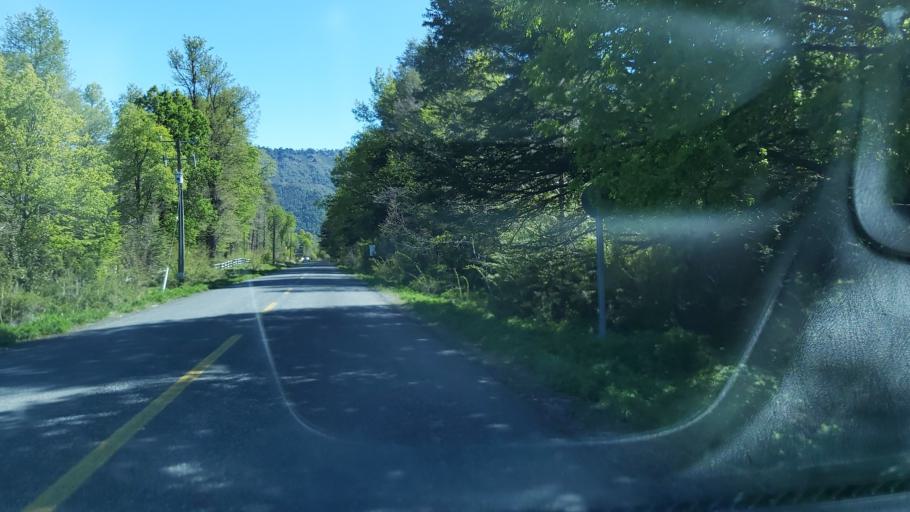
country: CL
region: Araucania
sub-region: Provincia de Cautin
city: Vilcun
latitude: -38.4758
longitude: -71.5312
